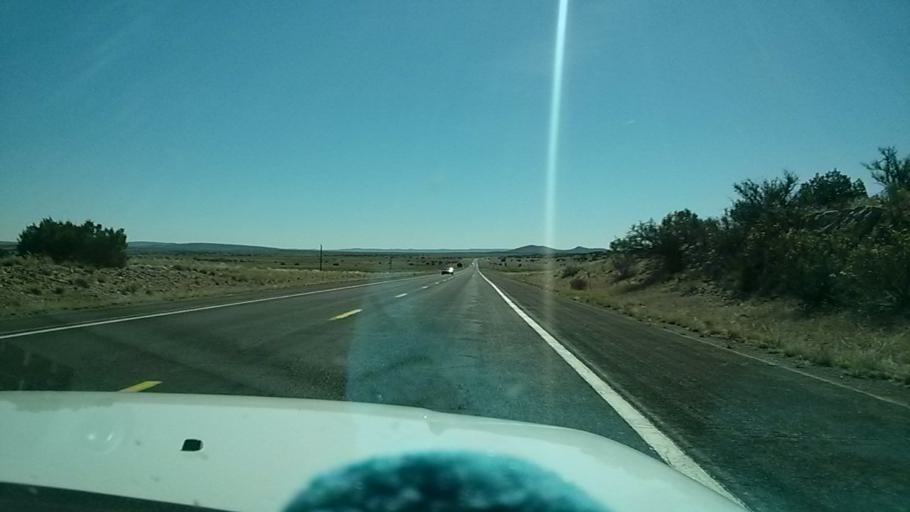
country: US
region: Arizona
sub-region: Mohave County
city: Peach Springs
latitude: 35.5526
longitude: -113.3474
